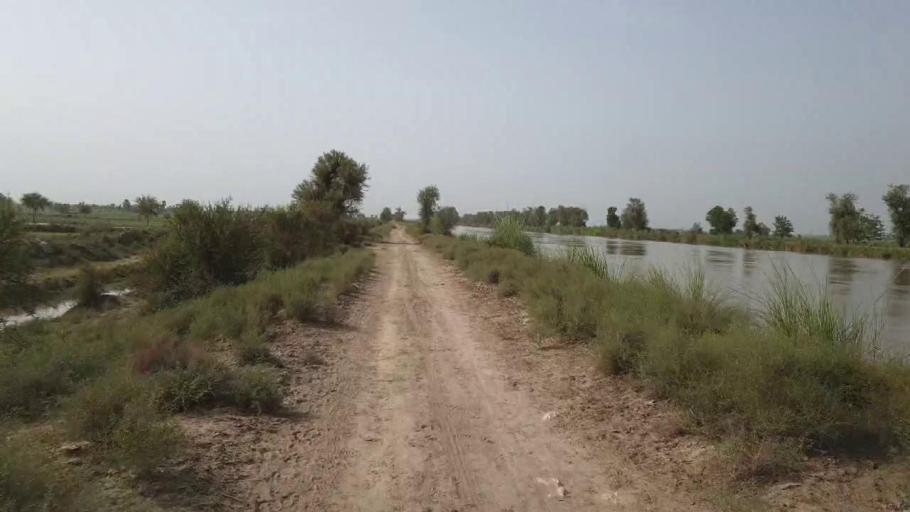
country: PK
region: Sindh
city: Daur
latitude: 26.4425
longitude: 68.1612
